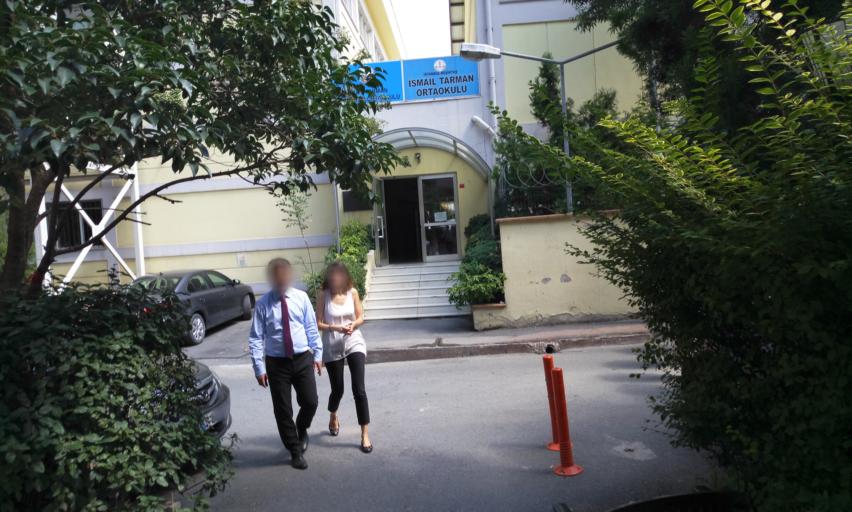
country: TR
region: Istanbul
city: Sisli
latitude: 41.0858
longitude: 29.0087
